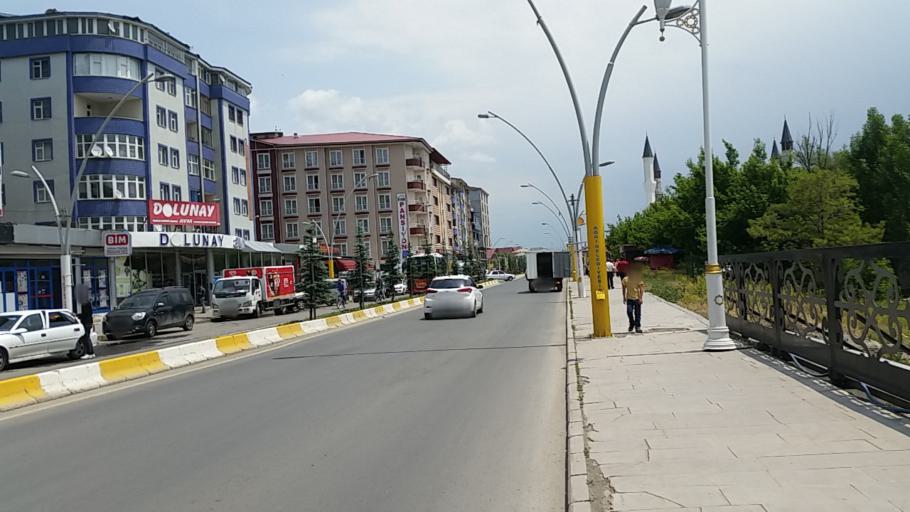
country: TR
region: Agri
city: Agri
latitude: 39.7188
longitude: 43.0312
